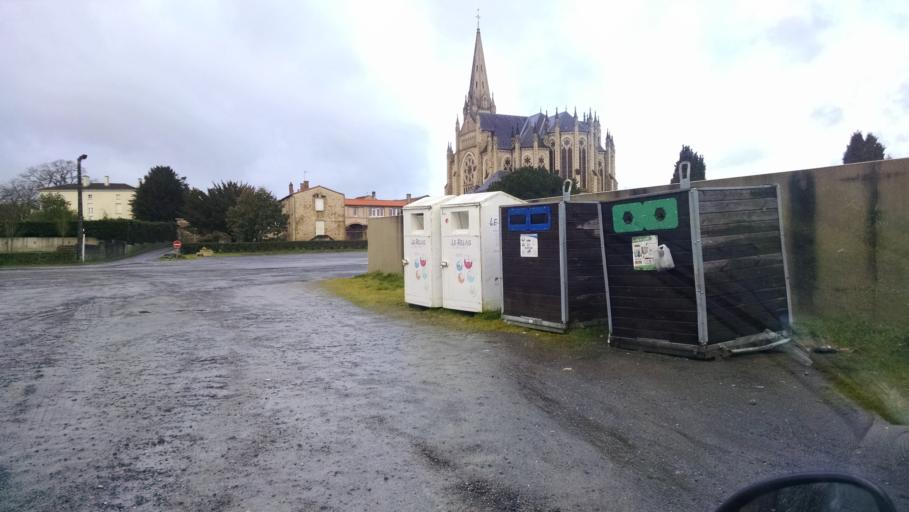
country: FR
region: Pays de la Loire
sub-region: Departement de la Loire-Atlantique
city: Aigrefeuille-sur-Maine
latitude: 47.0775
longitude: -1.3972
